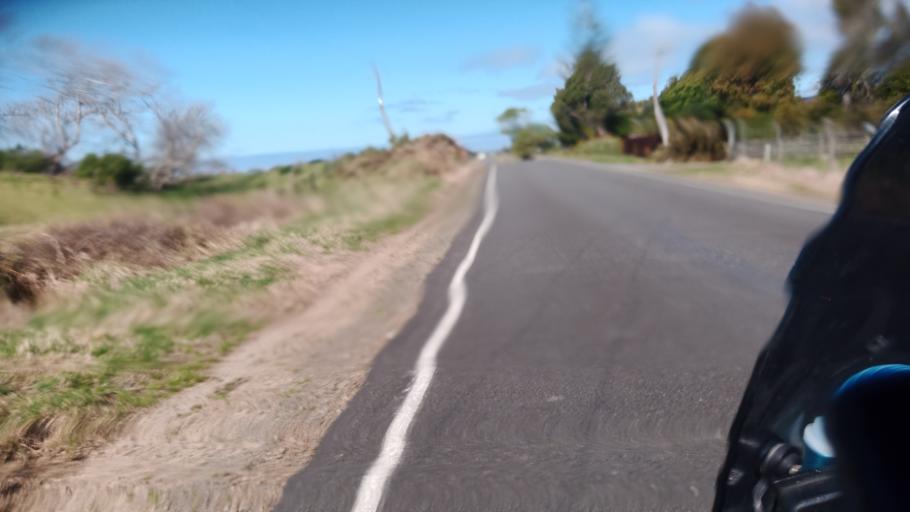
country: NZ
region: Gisborne
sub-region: Gisborne District
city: Gisborne
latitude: -39.0450
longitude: 177.8610
